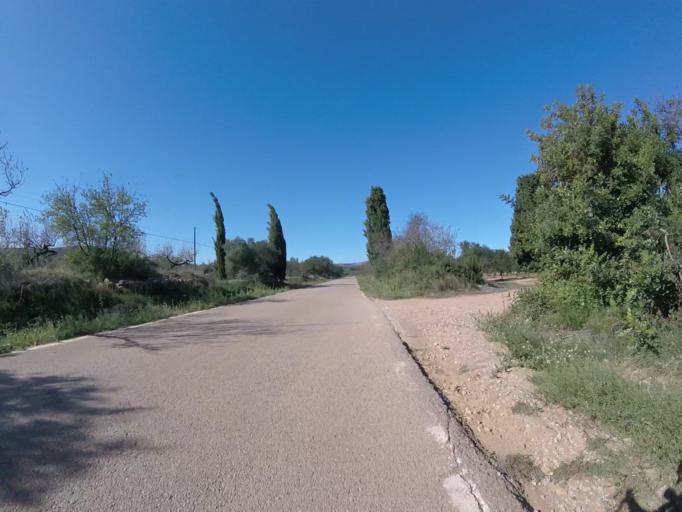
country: ES
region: Valencia
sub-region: Provincia de Castello
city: Chert/Xert
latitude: 40.4509
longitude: 0.1193
